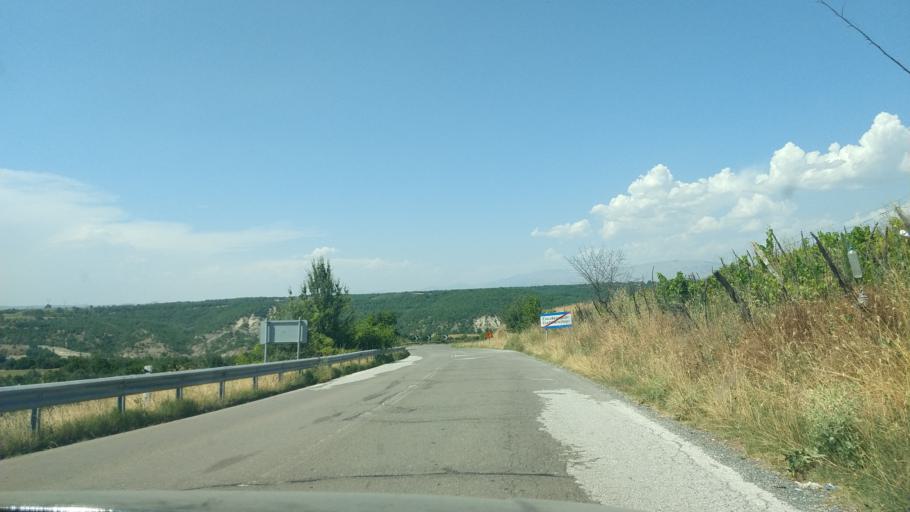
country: GR
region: West Macedonia
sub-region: Nomos Grevenon
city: Grevena
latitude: 40.0405
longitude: 21.4811
